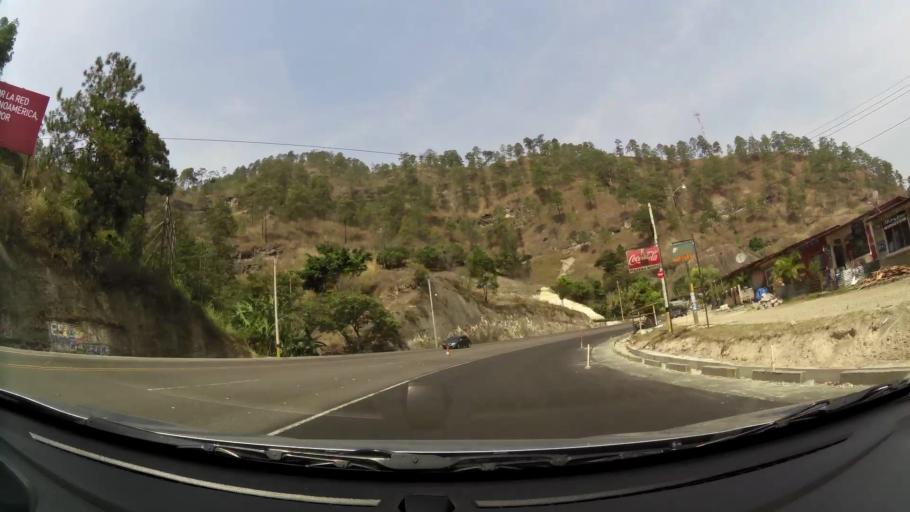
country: HN
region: Comayagua
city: Potrerillos
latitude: 14.5304
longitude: -87.8052
